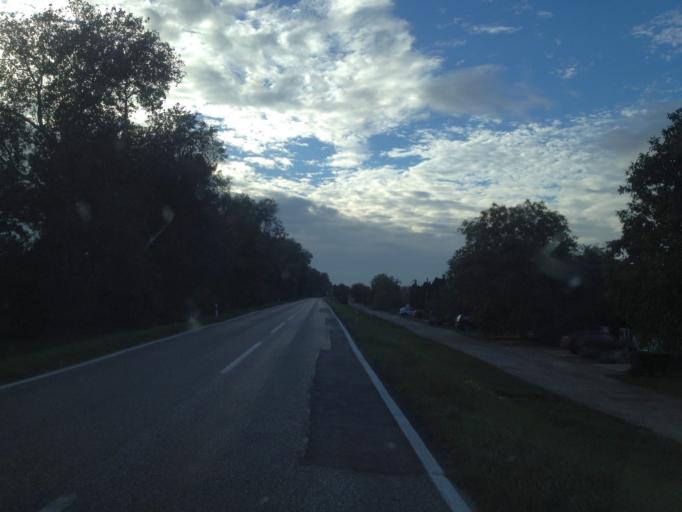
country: HU
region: Komarom-Esztergom
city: Almasfuzito
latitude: 47.7394
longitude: 18.2853
